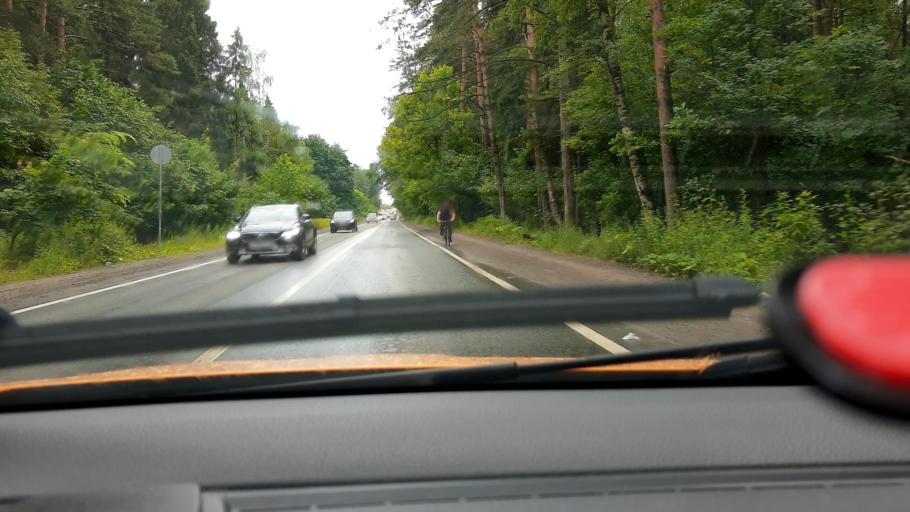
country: RU
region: Moskovskaya
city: Pirogovskiy
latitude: 55.9943
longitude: 37.7276
